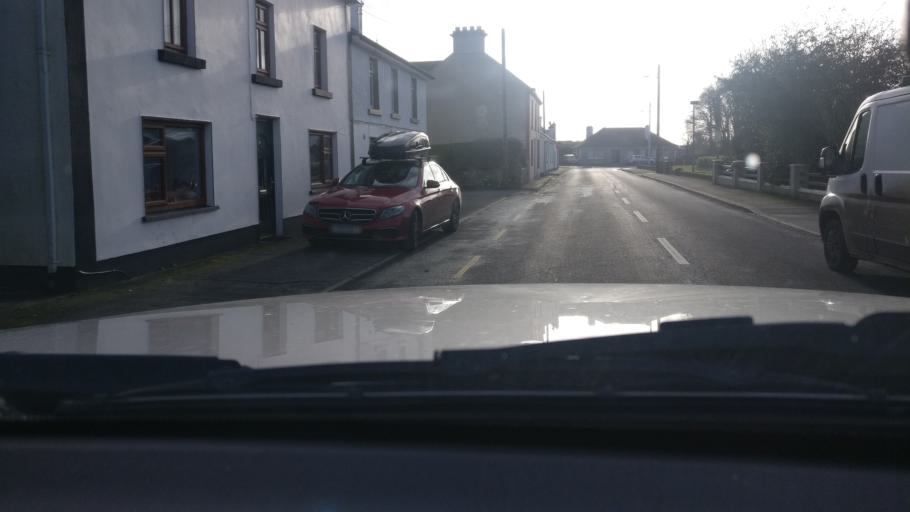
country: IE
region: Connaught
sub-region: County Galway
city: Ballinasloe
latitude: 53.2366
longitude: -8.2718
